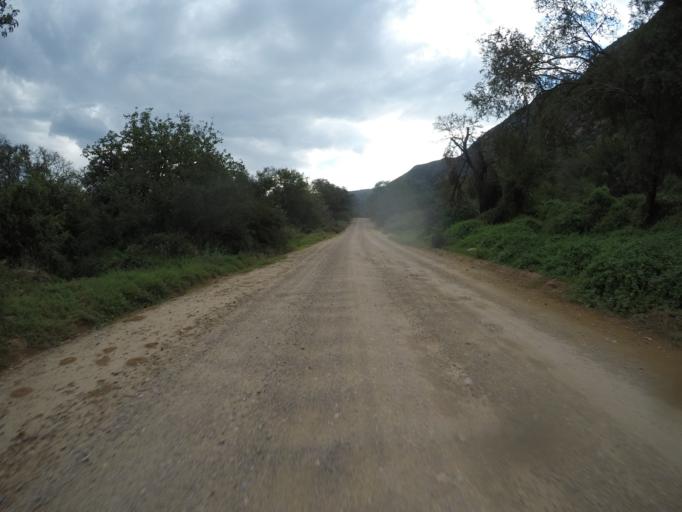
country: ZA
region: Eastern Cape
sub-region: Cacadu District Municipality
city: Kareedouw
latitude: -33.5765
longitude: 24.1429
